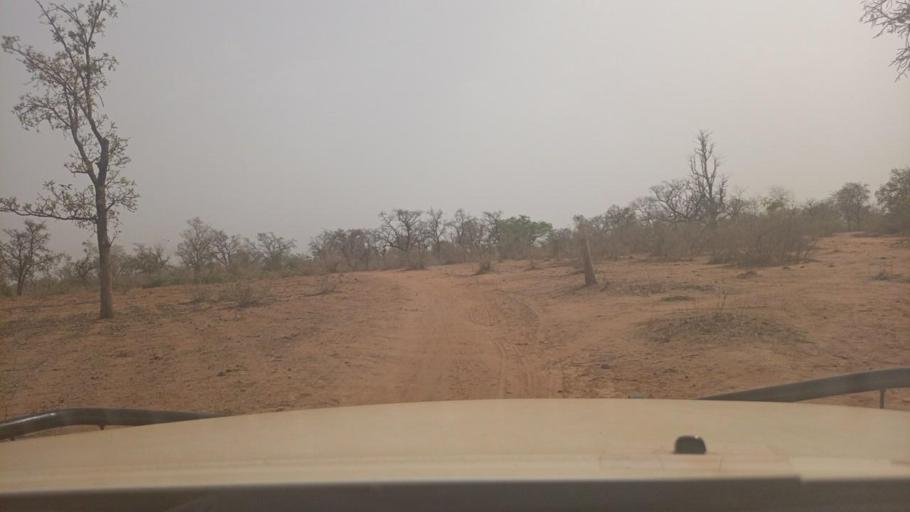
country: BF
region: Boucle du Mouhoun
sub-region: Province des Banwa
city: Salanso
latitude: 12.1576
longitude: -4.2448
